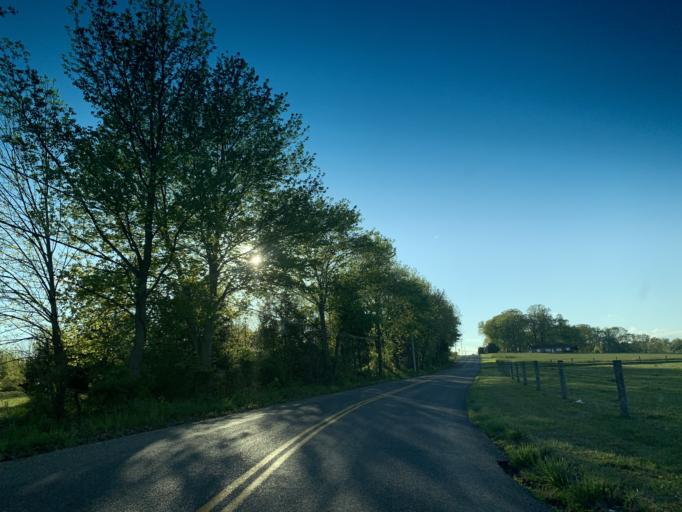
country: US
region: Maryland
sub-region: Harford County
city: Aberdeen
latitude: 39.5507
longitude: -76.1893
